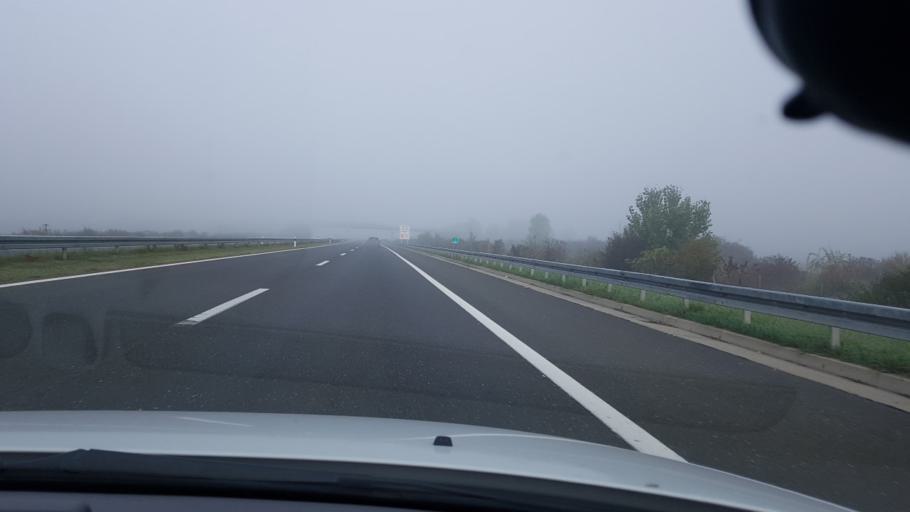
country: HR
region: Zagrebacka
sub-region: Grad Samobor
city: Samobor
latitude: 45.8154
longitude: 15.7599
